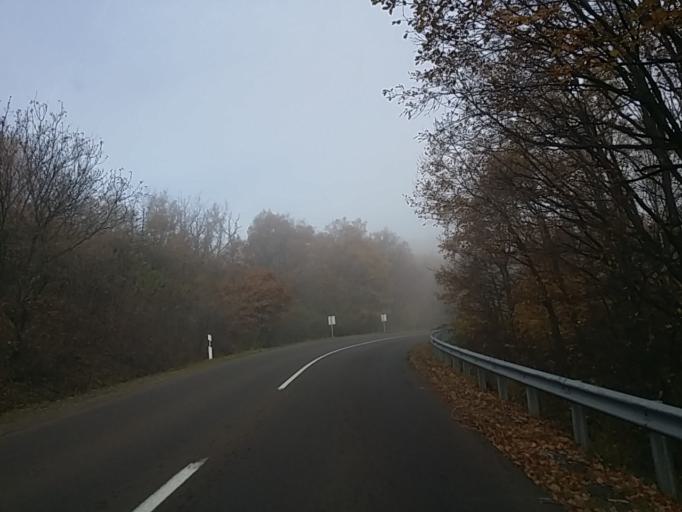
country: HU
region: Heves
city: Gyongyossolymos
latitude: 47.8378
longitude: 19.9628
